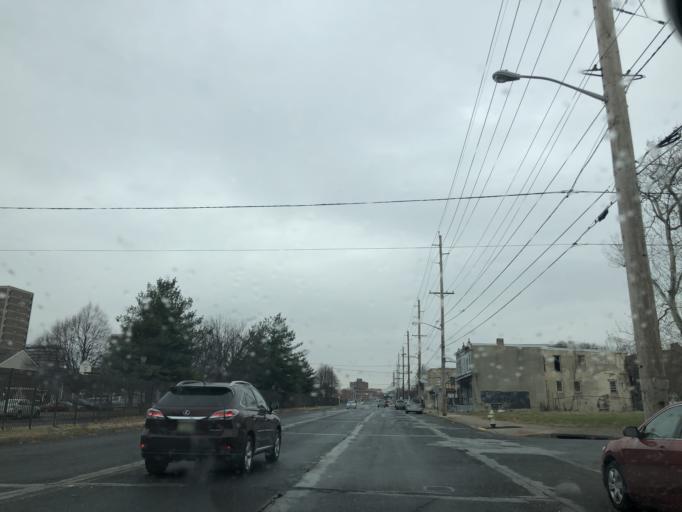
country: US
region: New Jersey
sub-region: Camden County
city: Camden
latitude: 39.9402
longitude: -75.1249
